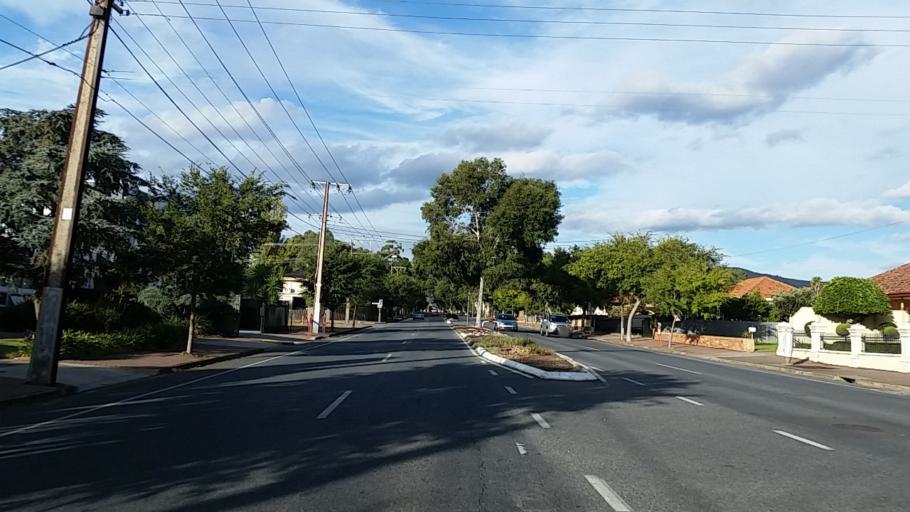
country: AU
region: South Australia
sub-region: Campbelltown
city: Campbelltown
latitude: -34.8889
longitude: 138.6673
